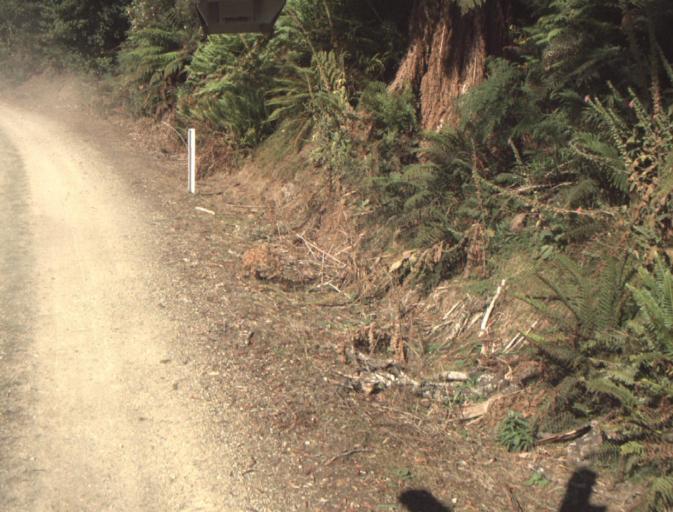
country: AU
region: Tasmania
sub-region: Dorset
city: Scottsdale
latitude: -41.2740
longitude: 147.3631
